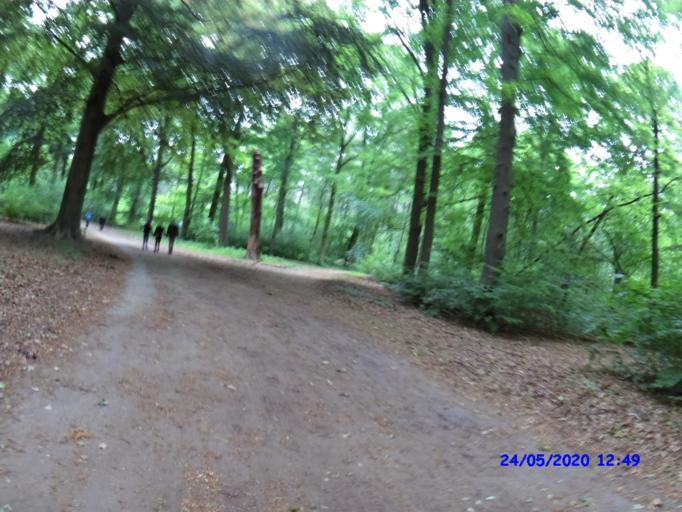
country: BE
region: Flanders
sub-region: Provincie Antwerpen
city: Retie
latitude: 51.2294
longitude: 5.0466
